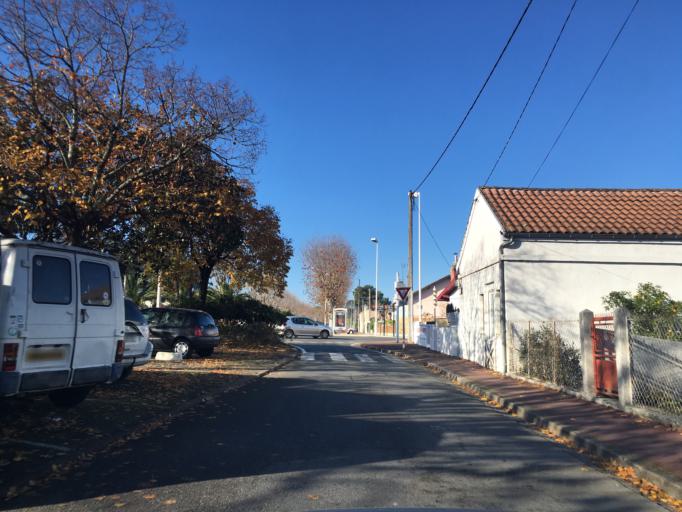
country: FR
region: Aquitaine
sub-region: Departement de la Gironde
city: Arcachon
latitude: 44.6535
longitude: -1.1459
